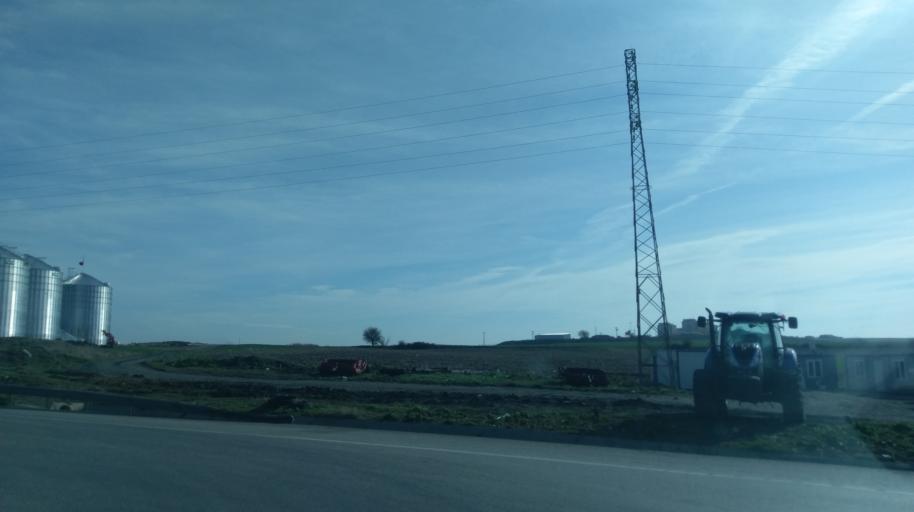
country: TR
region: Edirne
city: Uzun Keupru
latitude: 41.2345
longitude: 26.6878
